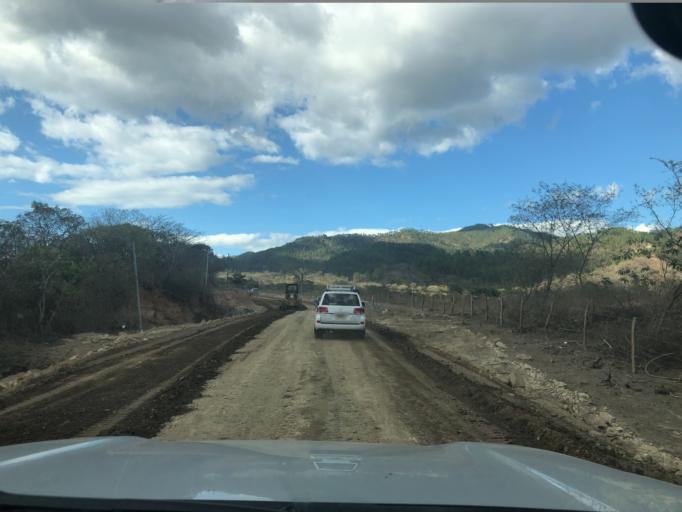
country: NI
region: Nueva Segovia
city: Ocotal
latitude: 13.6606
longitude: -86.6134
